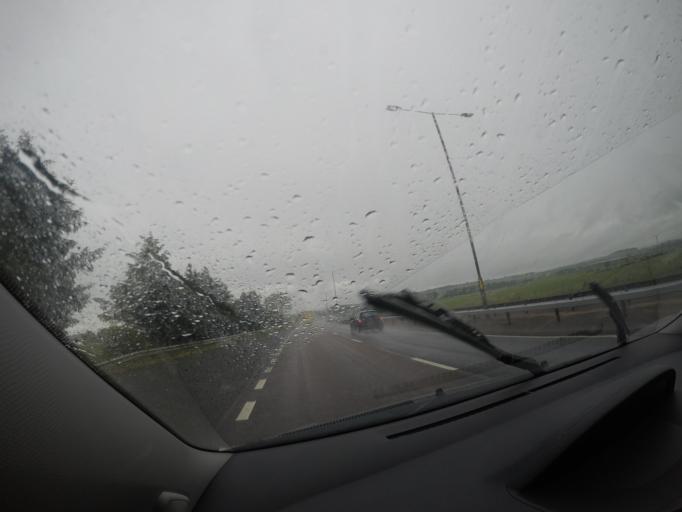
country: GB
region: Scotland
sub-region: Dundee City
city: Dundee
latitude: 56.5280
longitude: -2.9441
